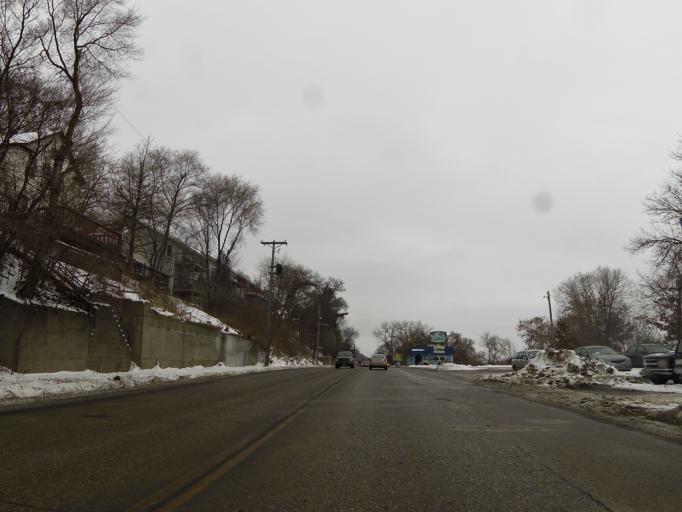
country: US
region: Minnesota
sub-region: Dakota County
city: South Saint Paul
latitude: 44.8999
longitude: -93.0401
